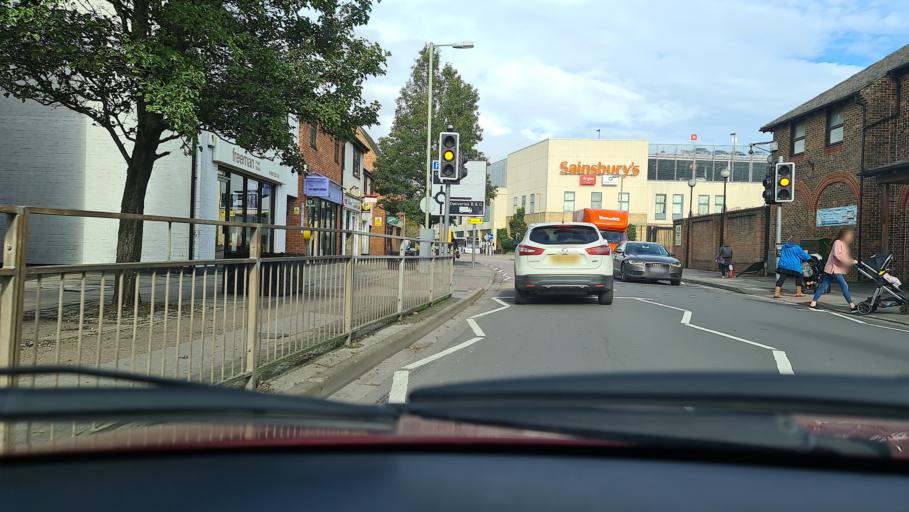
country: GB
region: England
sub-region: Oxfordshire
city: Bicester
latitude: 51.8968
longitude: -1.1520
